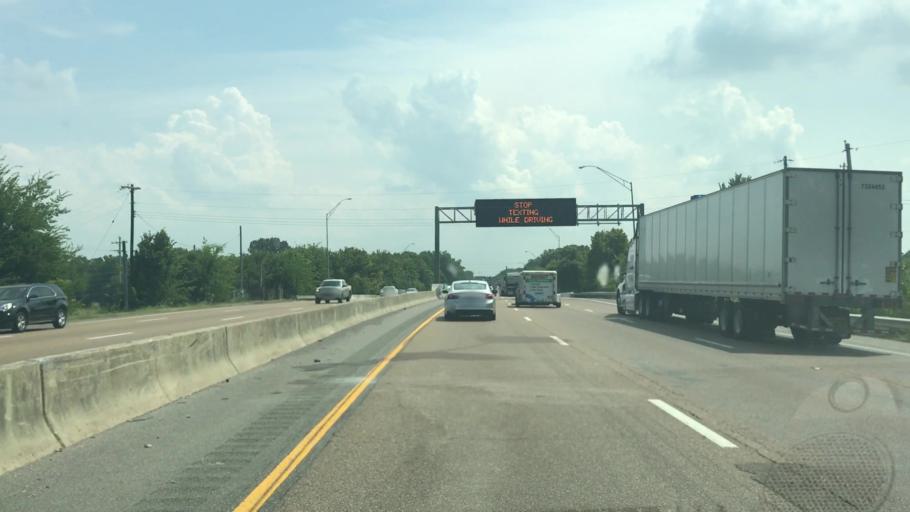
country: US
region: Tennessee
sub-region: Shelby County
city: Memphis
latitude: 35.1819
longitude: -90.0180
